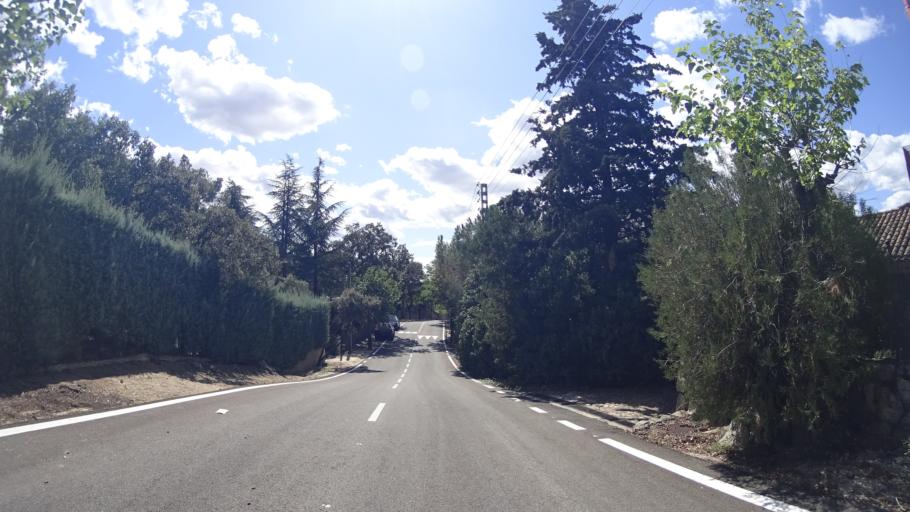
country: ES
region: Madrid
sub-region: Provincia de Madrid
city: Torrelodones
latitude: 40.5662
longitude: -3.9452
